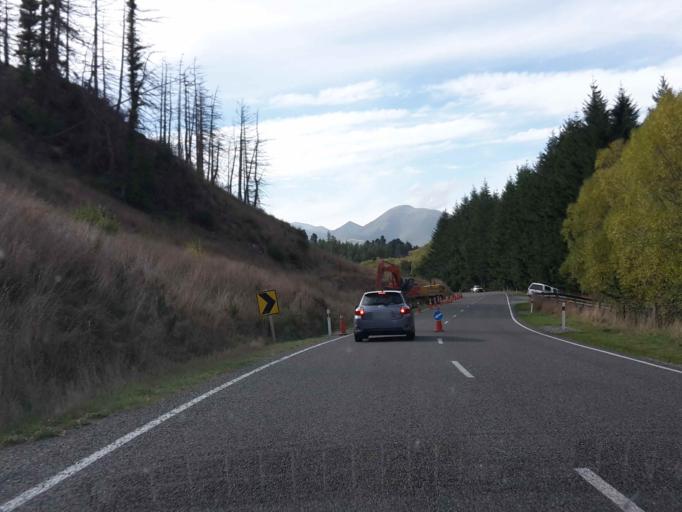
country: NZ
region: Canterbury
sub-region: Timaru District
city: Pleasant Point
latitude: -44.0598
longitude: 170.6747
